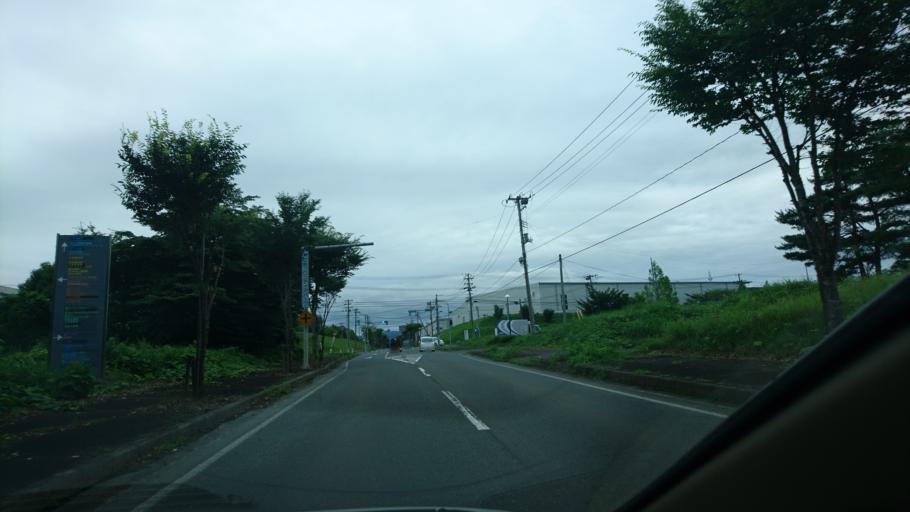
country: JP
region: Iwate
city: Mizusawa
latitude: 39.2087
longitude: 141.1780
